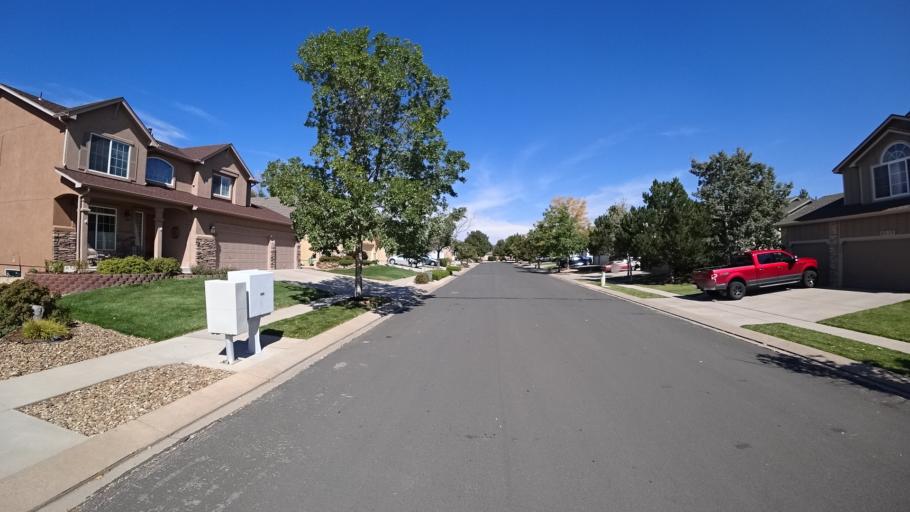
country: US
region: Colorado
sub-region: El Paso County
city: Cimarron Hills
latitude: 38.8951
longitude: -104.7054
